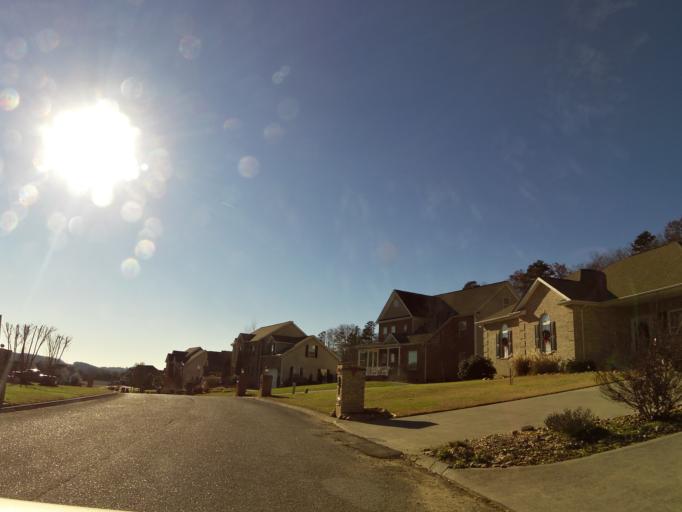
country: US
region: Tennessee
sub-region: Knox County
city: Knoxville
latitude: 36.0423
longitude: -83.9681
